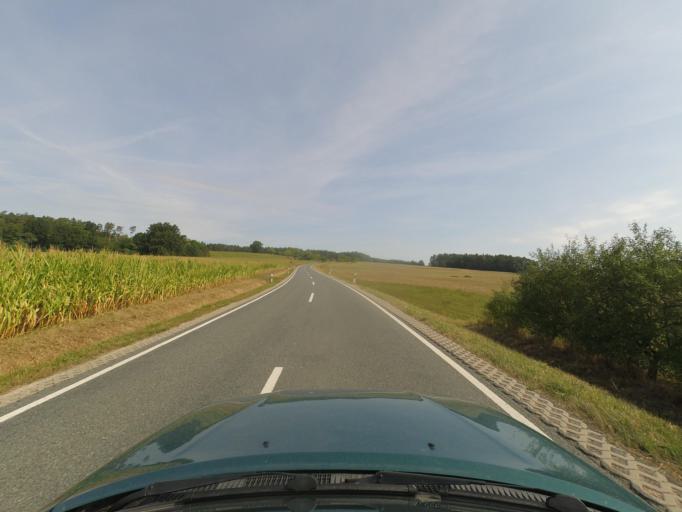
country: DE
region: Bavaria
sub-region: Regierungsbezirk Mittelfranken
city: Aurach
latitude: 49.2017
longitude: 10.4391
